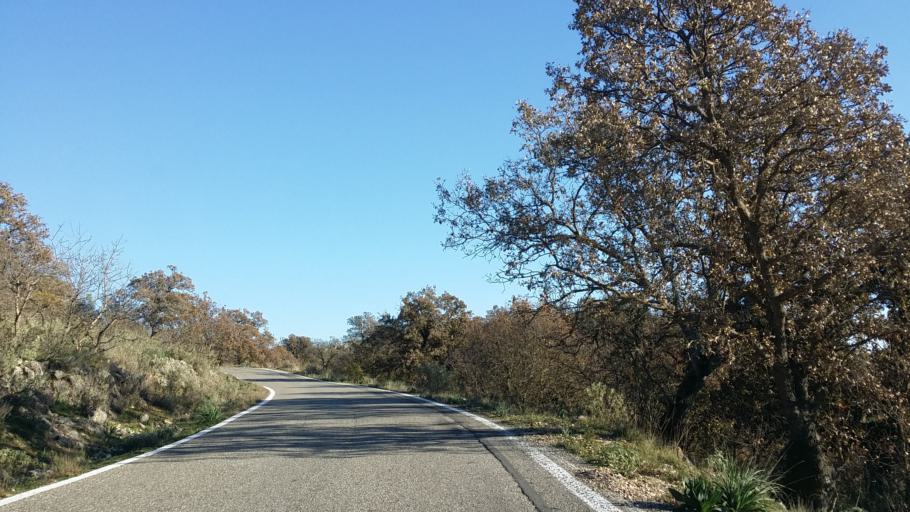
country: GR
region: West Greece
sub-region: Nomos Aitolias kai Akarnanias
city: Fitiai
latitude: 38.6355
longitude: 21.1932
